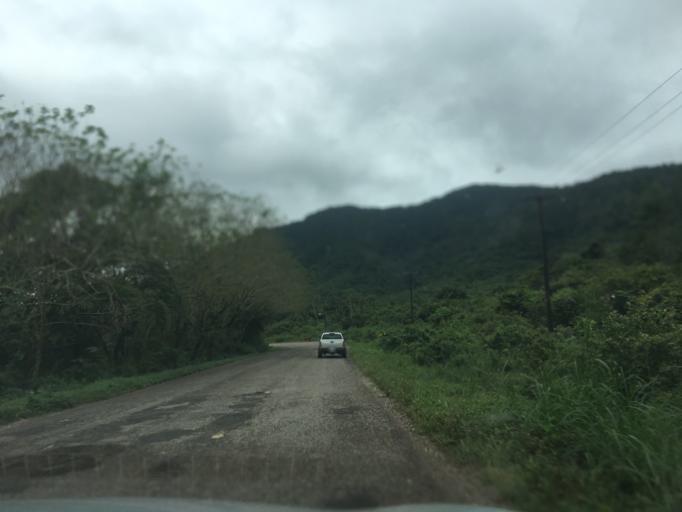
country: BZ
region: Cayo
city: Belmopan
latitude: 17.0541
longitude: -88.5710
